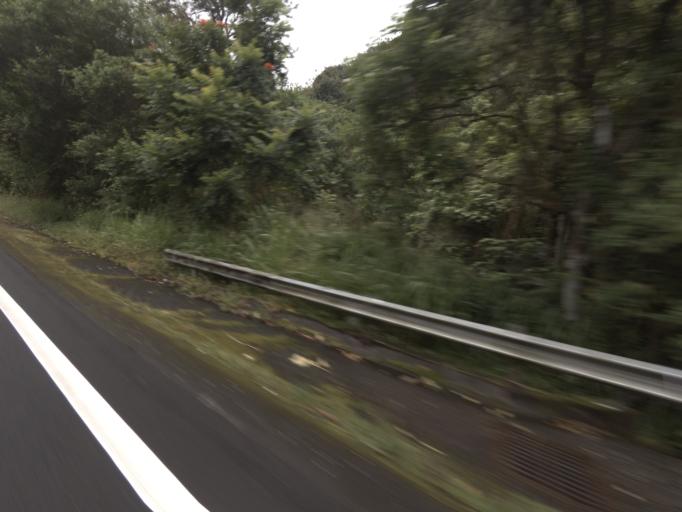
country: US
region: Hawaii
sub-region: Honolulu County
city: Kane'ohe
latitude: 21.3871
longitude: -157.8157
